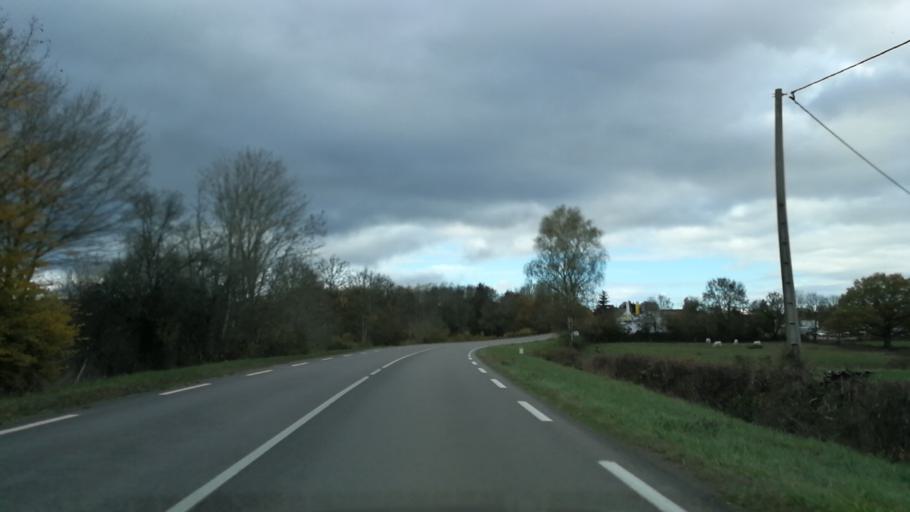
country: FR
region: Bourgogne
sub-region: Departement de la Cote-d'Or
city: Saulieu
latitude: 47.2719
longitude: 4.2504
